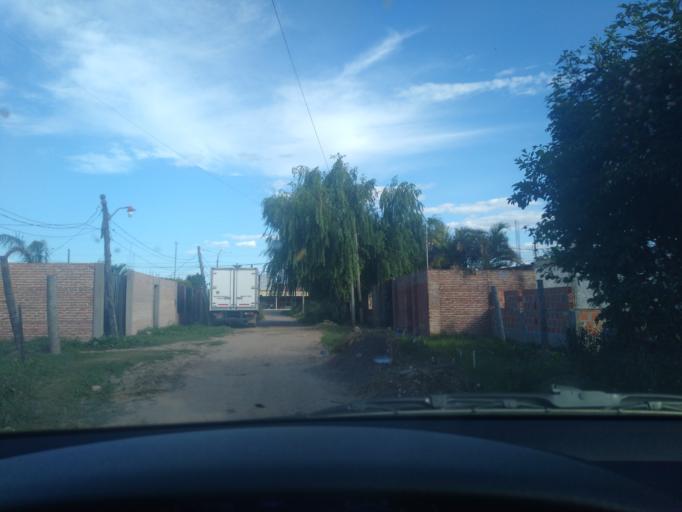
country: AR
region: Chaco
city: Barranqueras
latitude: -27.4722
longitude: -58.9255
